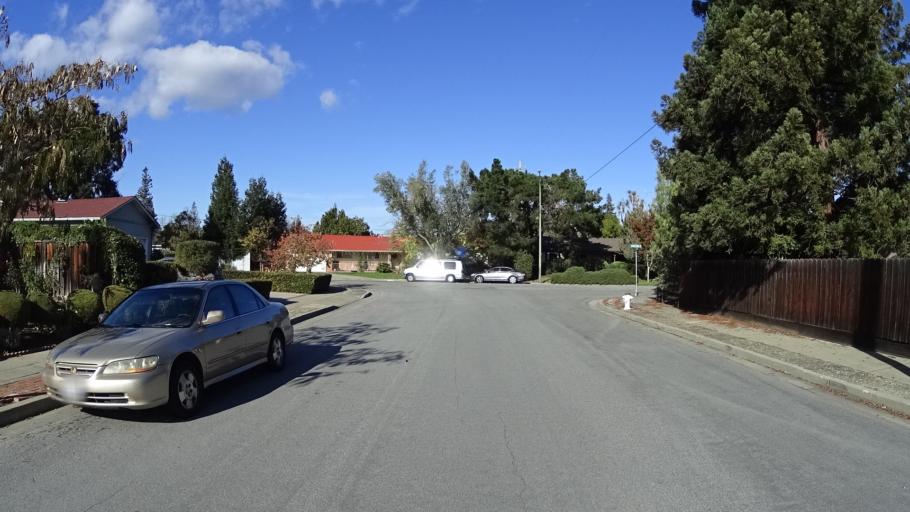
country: US
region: California
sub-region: Santa Clara County
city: Sunnyvale
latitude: 37.3459
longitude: -122.0542
